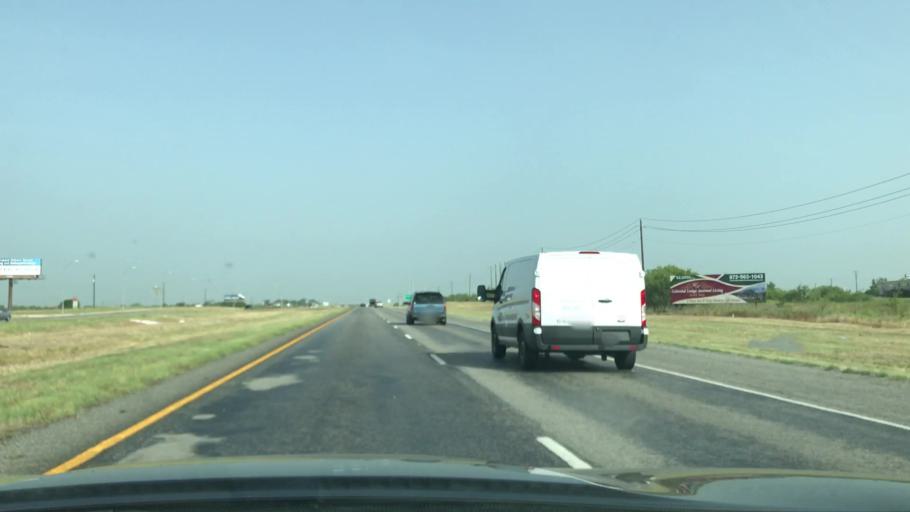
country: US
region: Texas
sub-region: Kaufman County
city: Terrell
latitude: 32.7237
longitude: -96.3258
